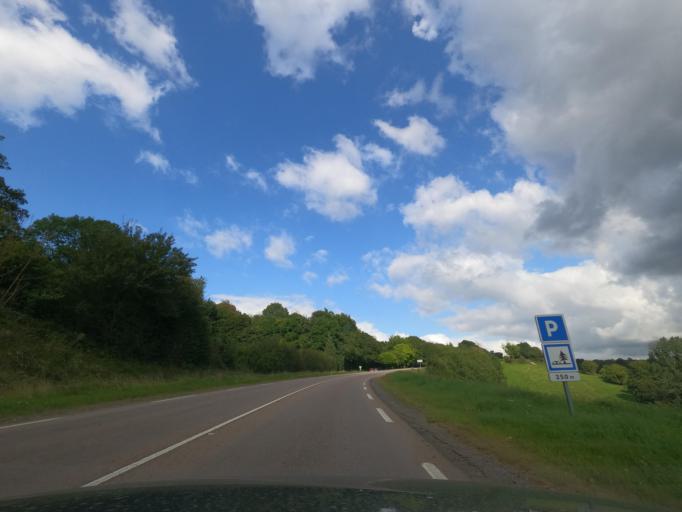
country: FR
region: Lower Normandy
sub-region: Departement de l'Orne
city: Gace
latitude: 48.8007
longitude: 0.3033
